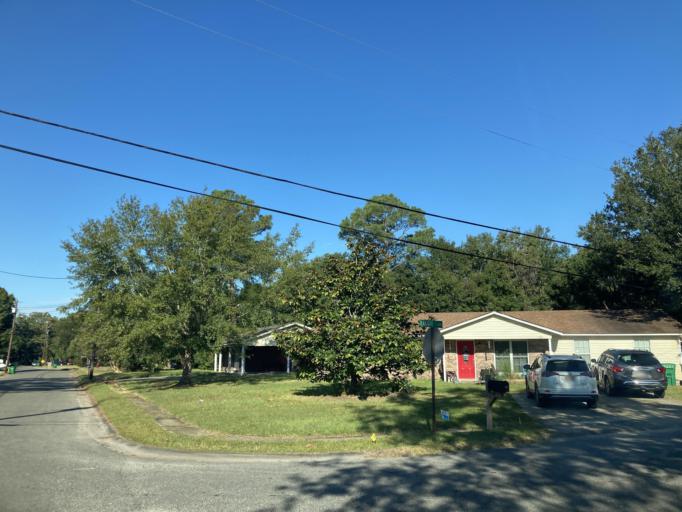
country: US
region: Mississippi
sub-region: Jackson County
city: Saint Martin
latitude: 30.4443
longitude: -88.8805
